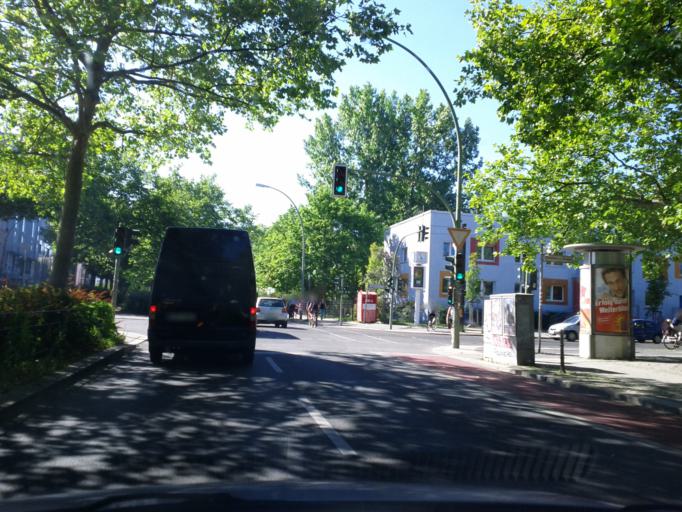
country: DE
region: Berlin
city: Prenzlauer Berg Bezirk
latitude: 52.5488
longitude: 13.4206
